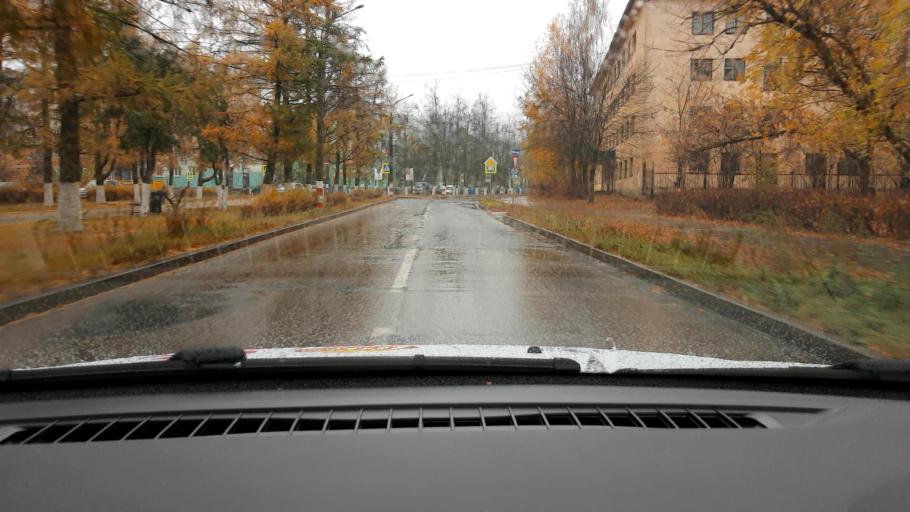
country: RU
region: Nizjnij Novgorod
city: Dzerzhinsk
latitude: 56.2387
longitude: 43.4434
